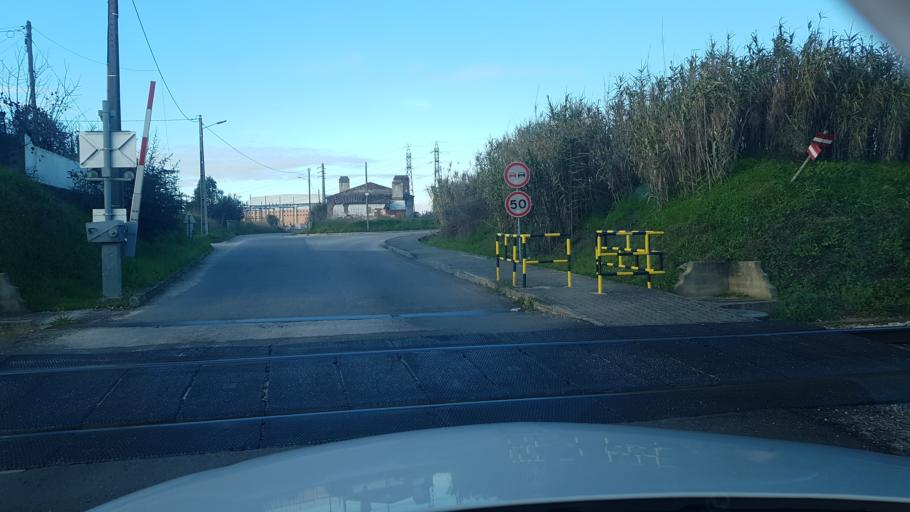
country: PT
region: Santarem
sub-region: Entroncamento
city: Entroncamento
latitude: 39.4682
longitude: -8.4666
